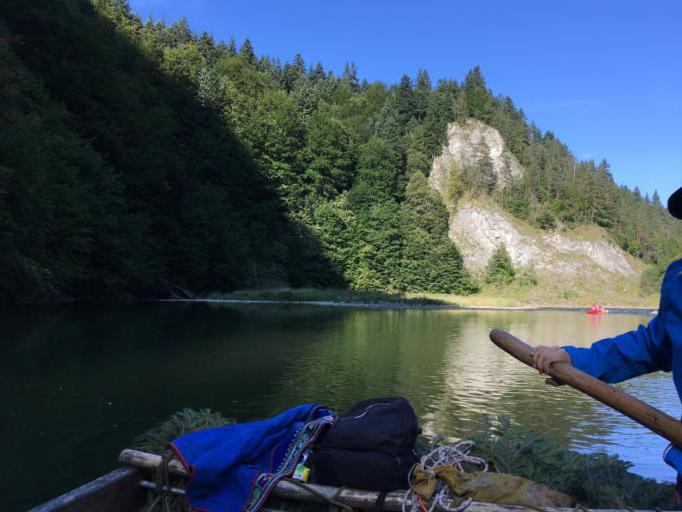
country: PL
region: Lesser Poland Voivodeship
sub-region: Powiat nowotarski
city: Kroscienko nad Dunajcem
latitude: 49.4167
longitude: 20.4463
